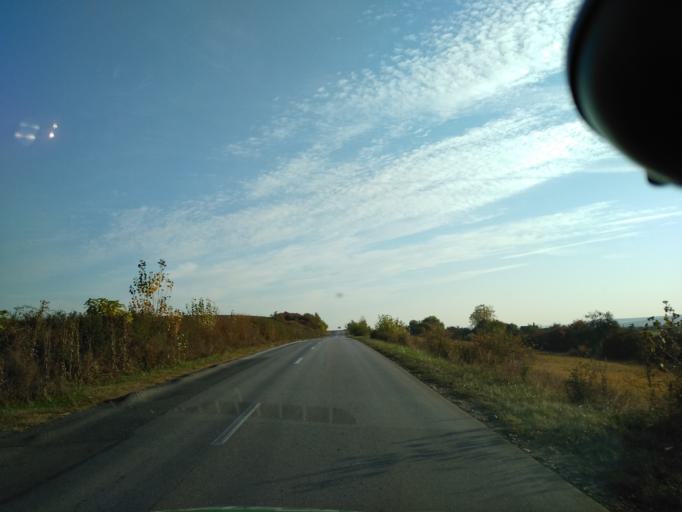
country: RO
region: Timis
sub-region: Comuna Fibis
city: Fibis
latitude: 45.9526
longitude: 21.4143
